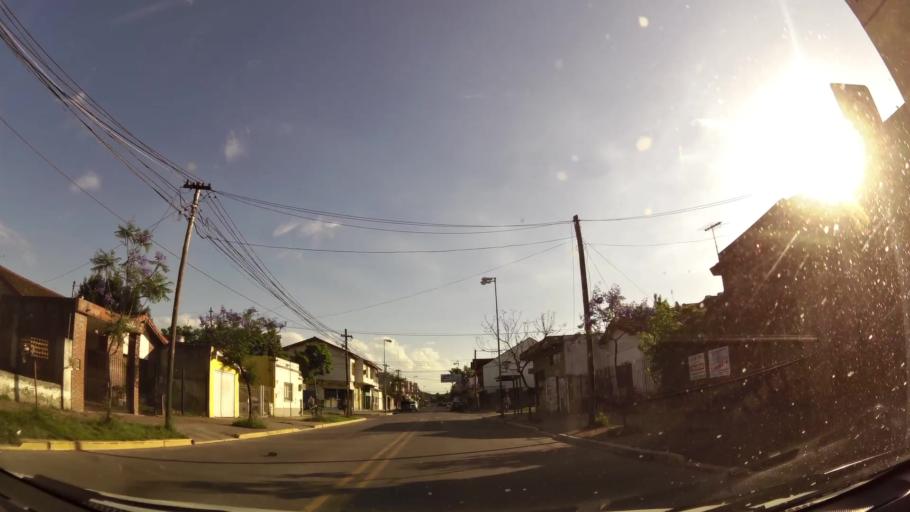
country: AR
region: Buenos Aires
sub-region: Partido de Merlo
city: Merlo
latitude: -34.6760
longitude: -58.7255
